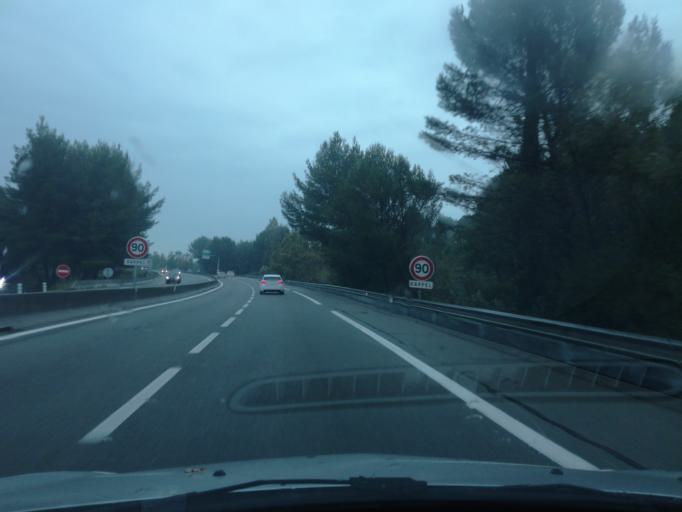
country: FR
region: Provence-Alpes-Cote d'Azur
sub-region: Departement des Alpes-Maritimes
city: Mougins
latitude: 43.5989
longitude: 7.0021
